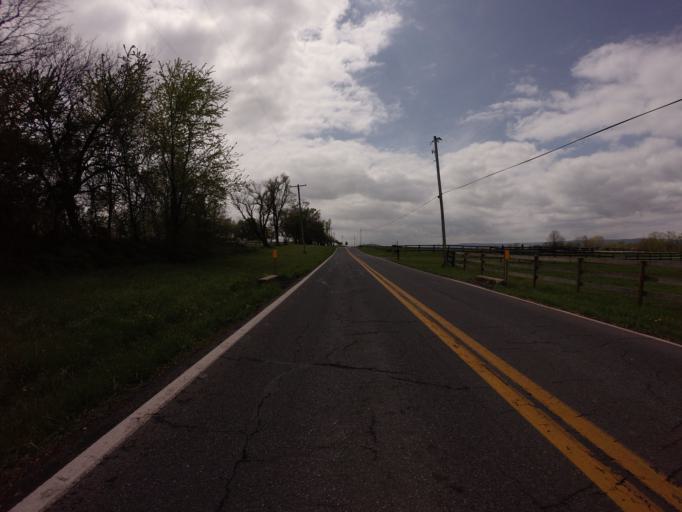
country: US
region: Maryland
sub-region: Frederick County
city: Thurmont
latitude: 39.6028
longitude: -77.3540
